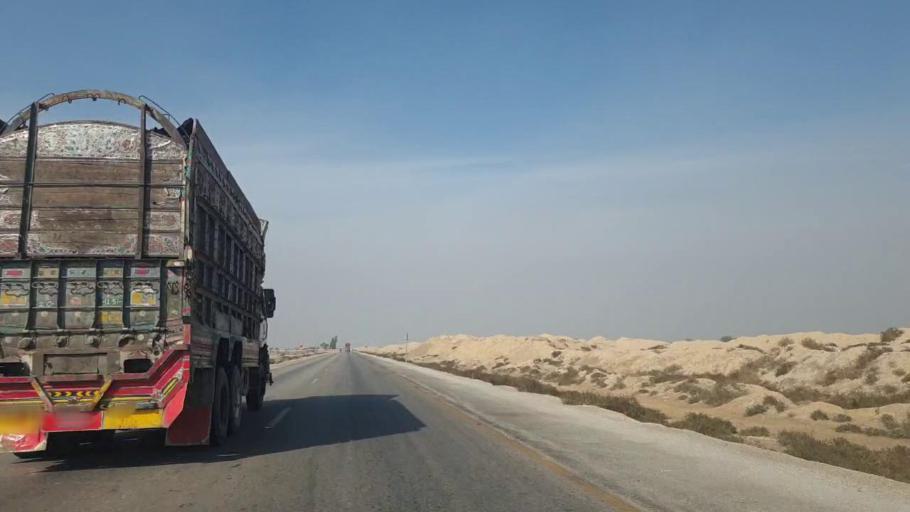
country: PK
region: Sindh
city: Sann
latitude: 25.9559
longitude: 68.1942
